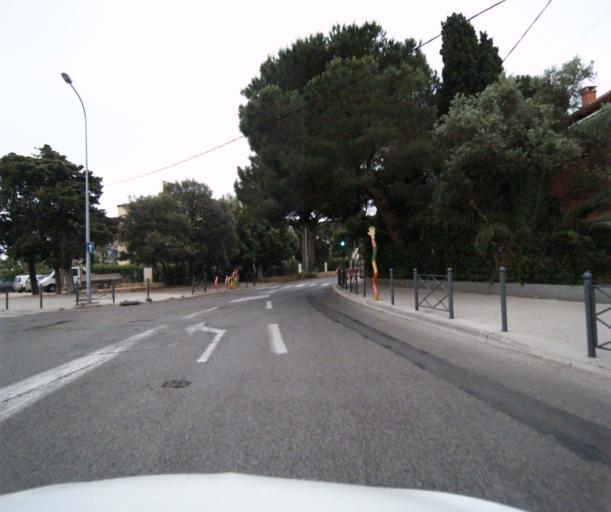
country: FR
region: Provence-Alpes-Cote d'Azur
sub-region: Departement du Var
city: La Seyne-sur-Mer
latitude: 43.0844
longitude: 5.8915
